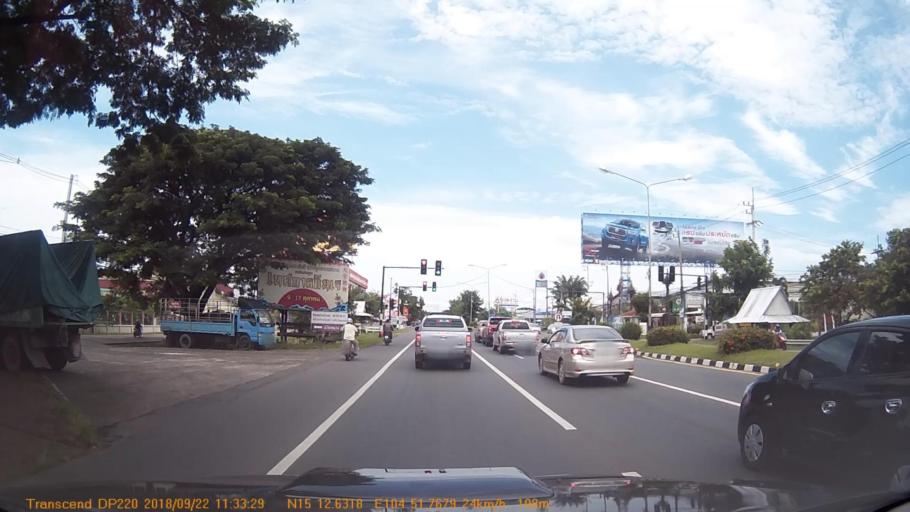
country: TH
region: Changwat Ubon Ratchathani
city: Warin Chamrap
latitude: 15.2105
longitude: 104.8628
